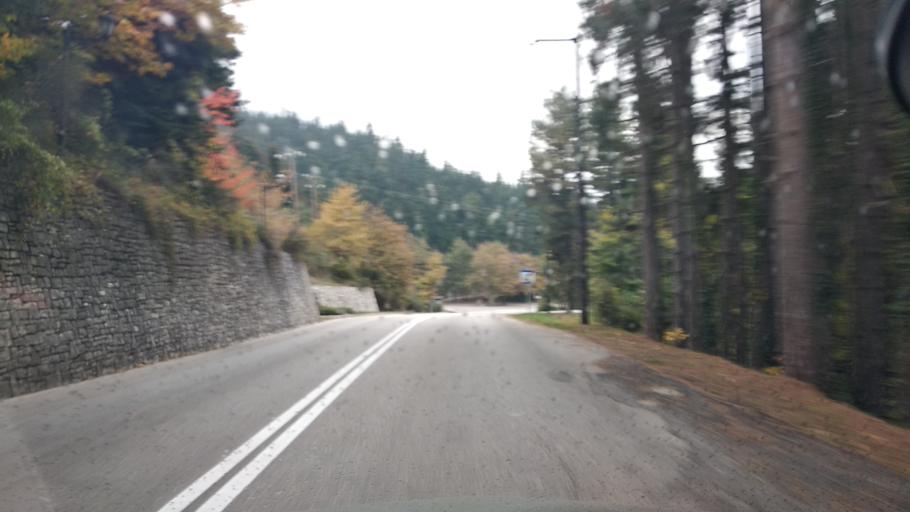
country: GR
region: Thessaly
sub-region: Trikala
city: Pyli
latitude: 39.4994
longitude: 21.5383
